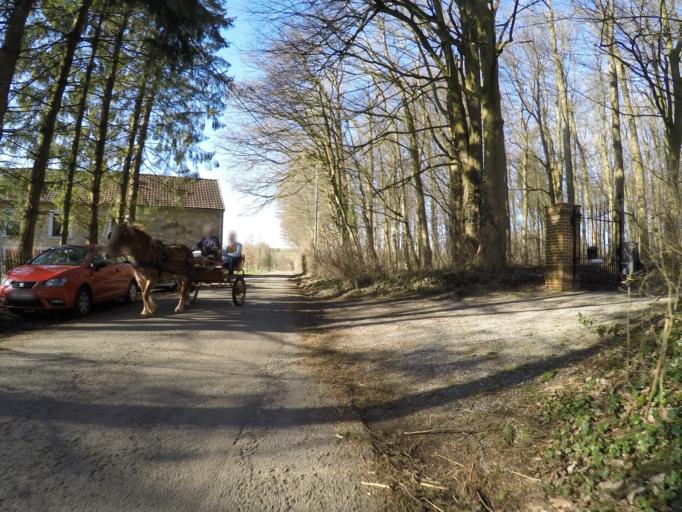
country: BE
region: Wallonia
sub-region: Province de Namur
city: Gesves
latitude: 50.3602
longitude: 5.0816
